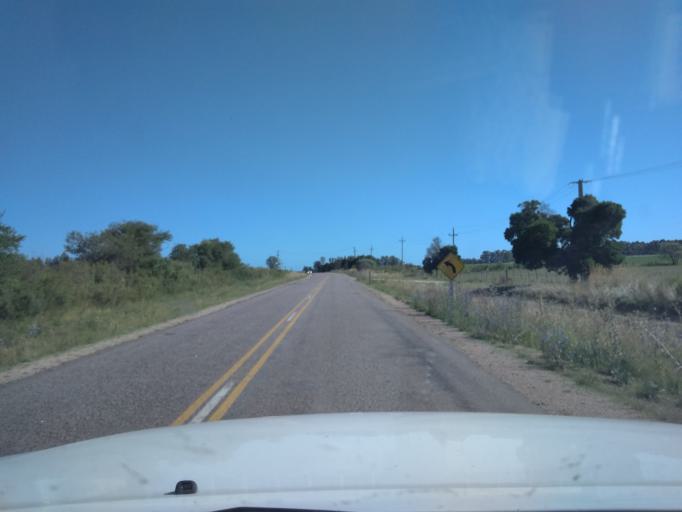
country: UY
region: Canelones
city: San Ramon
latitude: -34.2615
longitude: -55.9273
